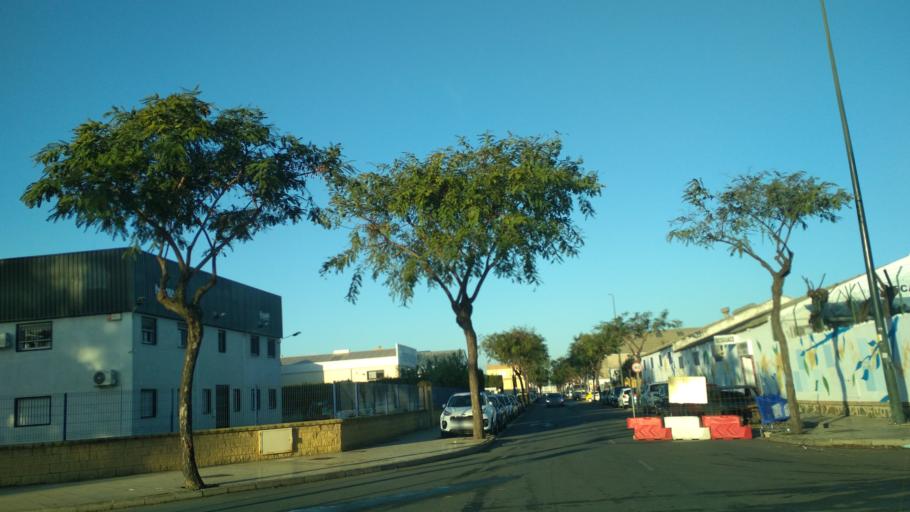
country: ES
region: Andalusia
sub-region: Provincia de Huelva
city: Huelva
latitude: 37.2416
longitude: -6.9476
